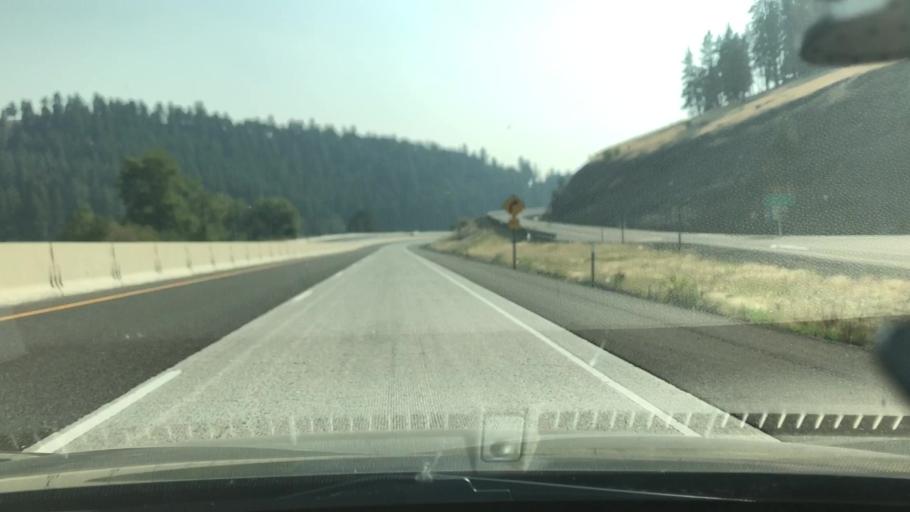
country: US
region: Oregon
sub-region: Union County
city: La Grande
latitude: 45.3446
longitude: -118.2255
